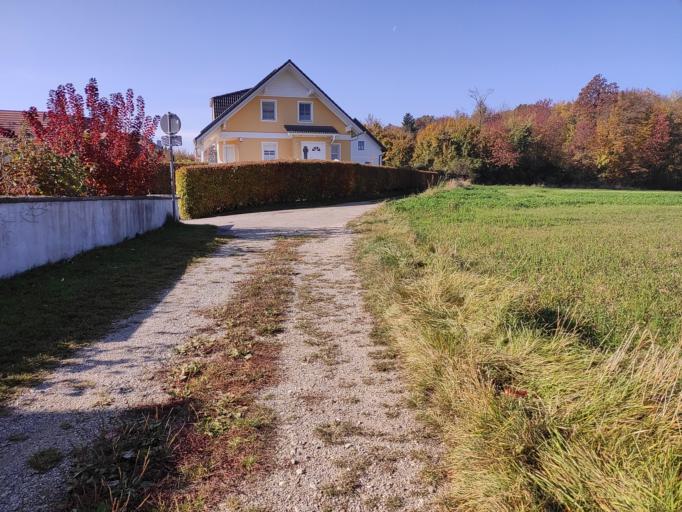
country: AT
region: Lower Austria
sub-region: Politischer Bezirk Sankt Polten
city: Pyhra
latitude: 48.1630
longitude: 15.6785
